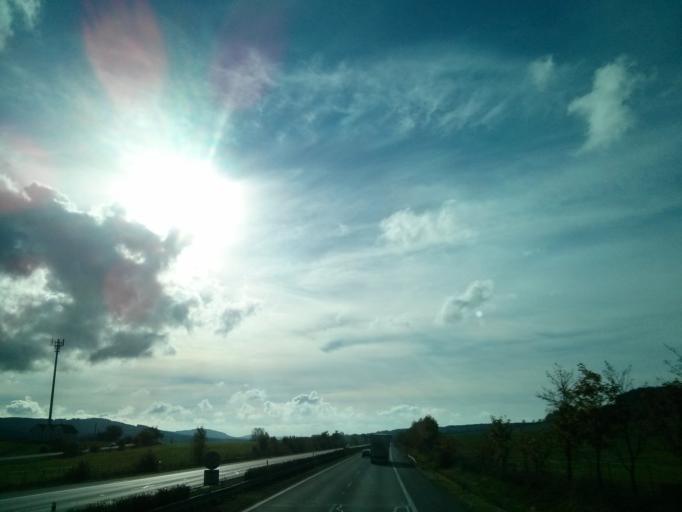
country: CZ
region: Plzensky
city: Myto
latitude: 49.7984
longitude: 13.7472
